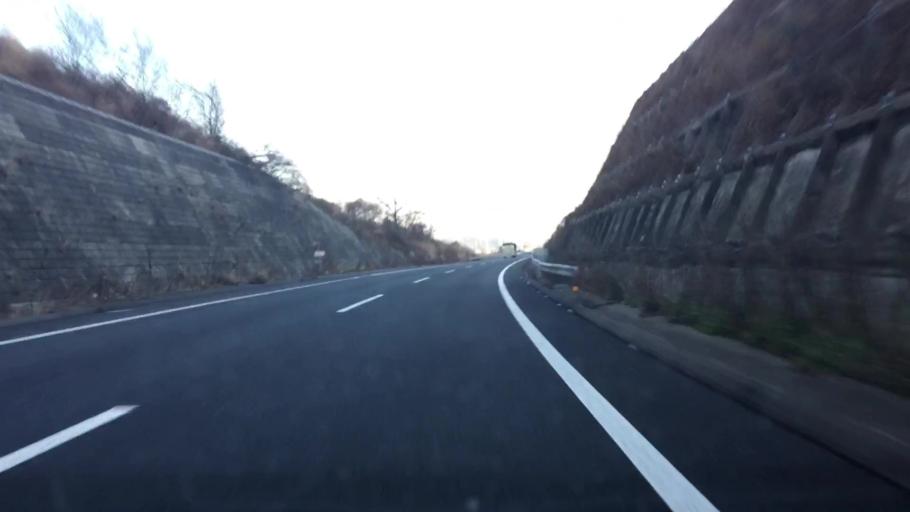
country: JP
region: Tochigi
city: Tanuma
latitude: 36.3718
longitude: 139.5403
